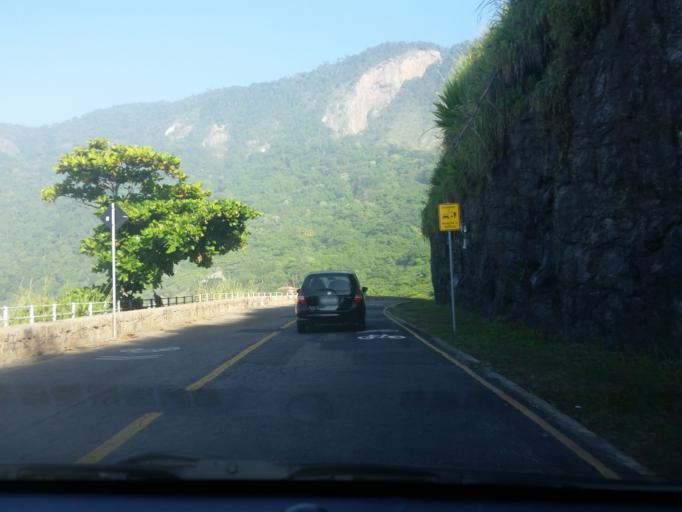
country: BR
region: Rio de Janeiro
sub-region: Nilopolis
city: Nilopolis
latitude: -23.0400
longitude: -43.5019
